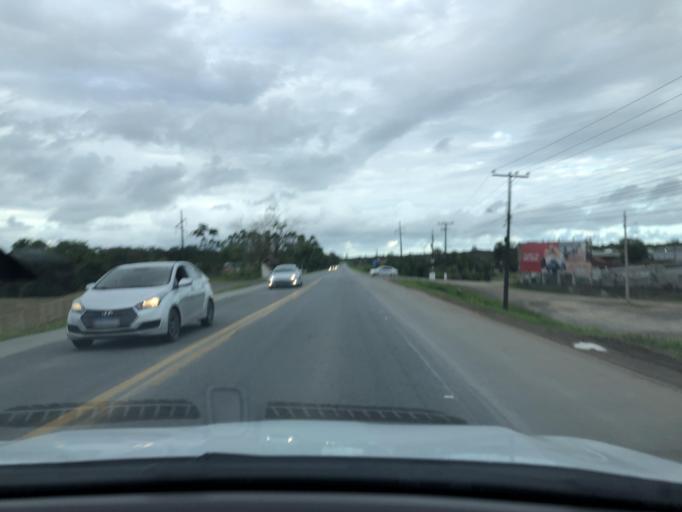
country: BR
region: Santa Catarina
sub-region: Joinville
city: Joinville
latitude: -26.4166
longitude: -48.7724
